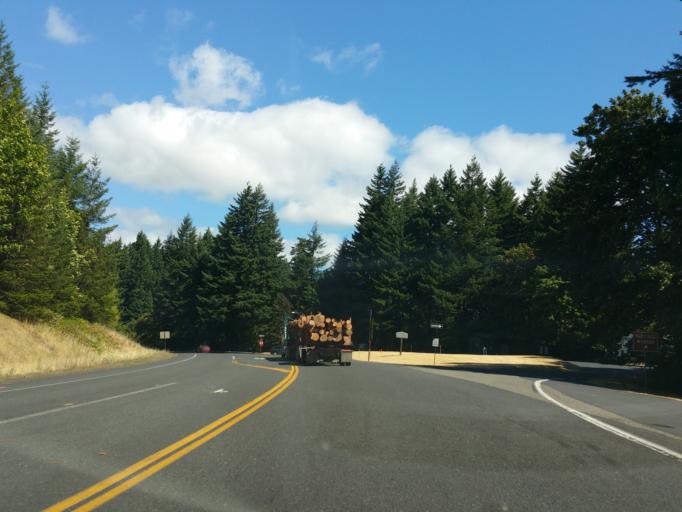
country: US
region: Oregon
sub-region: Hood River County
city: Cascade Locks
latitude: 45.6635
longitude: -121.9050
